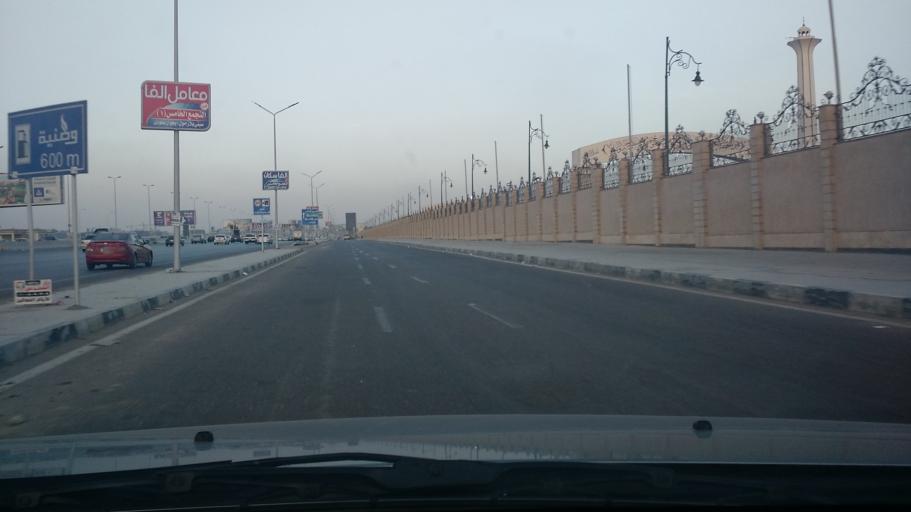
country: EG
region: Muhafazat al Qahirah
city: Cairo
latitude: 30.0196
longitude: 31.3811
